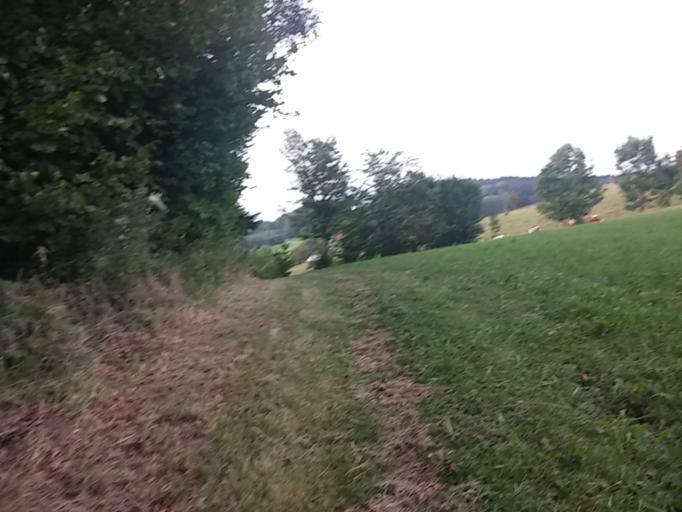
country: DE
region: Bavaria
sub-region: Swabia
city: Woringen
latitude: 47.8691
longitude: 10.1948
